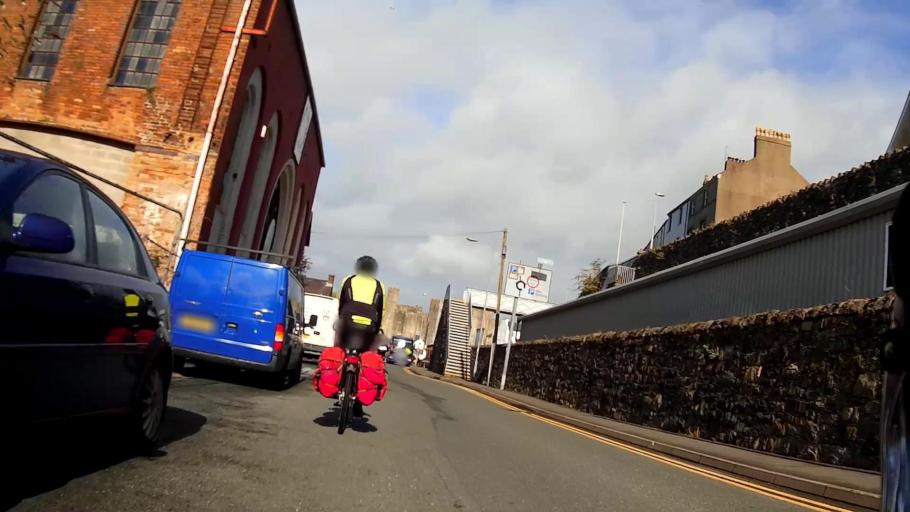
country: GB
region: Wales
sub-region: Gwynedd
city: Caernarfon
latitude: 53.1374
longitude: -4.2720
